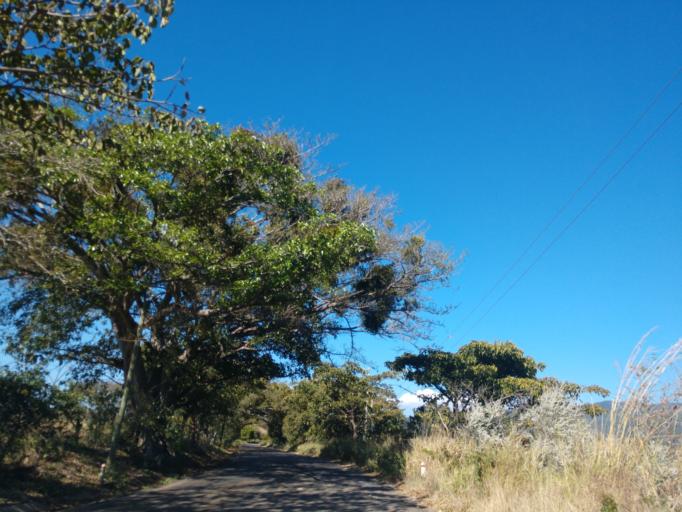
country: MX
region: Nayarit
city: Compostela
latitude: 21.2583
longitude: -104.8977
